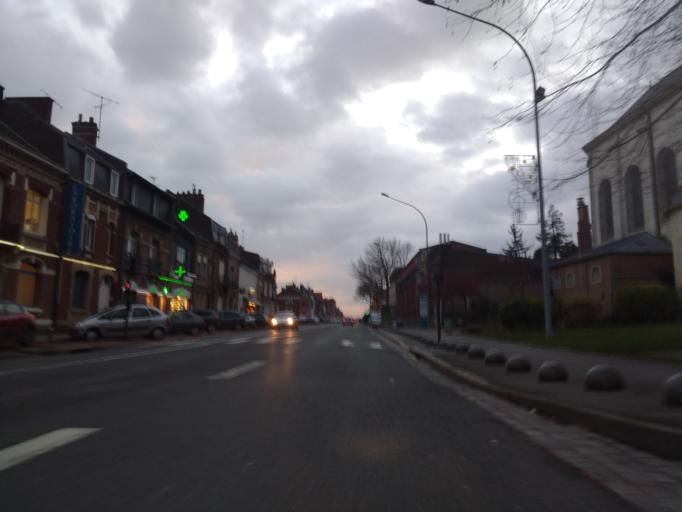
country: FR
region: Picardie
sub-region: Departement de la Somme
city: Rivery
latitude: 49.8836
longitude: 2.3244
